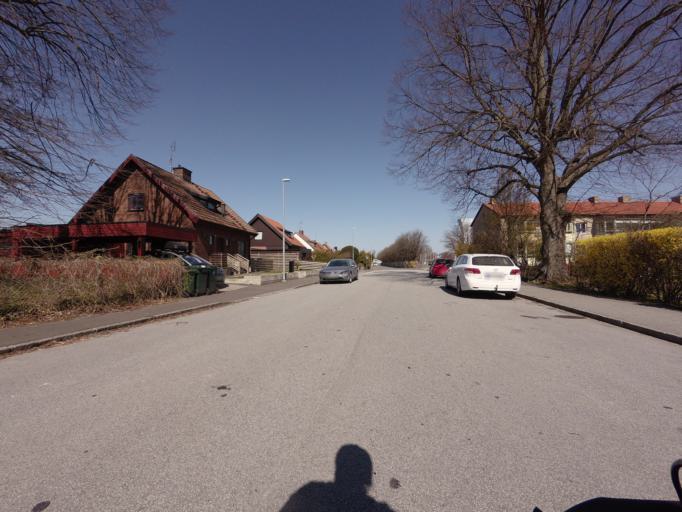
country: SE
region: Skane
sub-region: Vellinge Kommun
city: Vellinge
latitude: 55.4706
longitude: 13.0244
